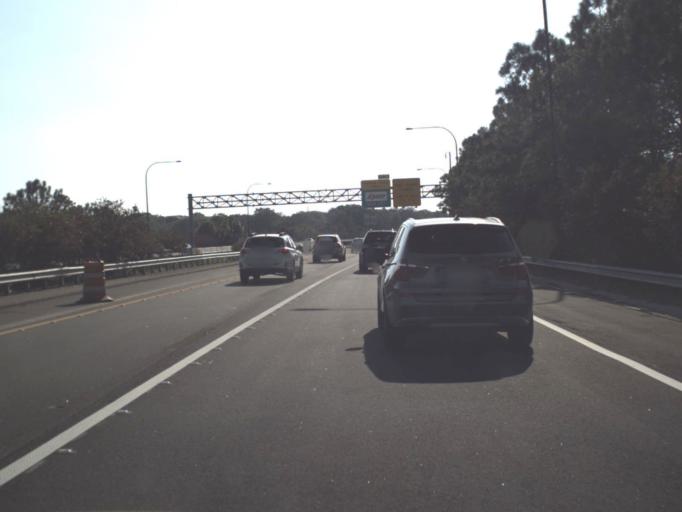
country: US
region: Florida
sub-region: Orange County
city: Orlovista
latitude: 28.5485
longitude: -81.4733
